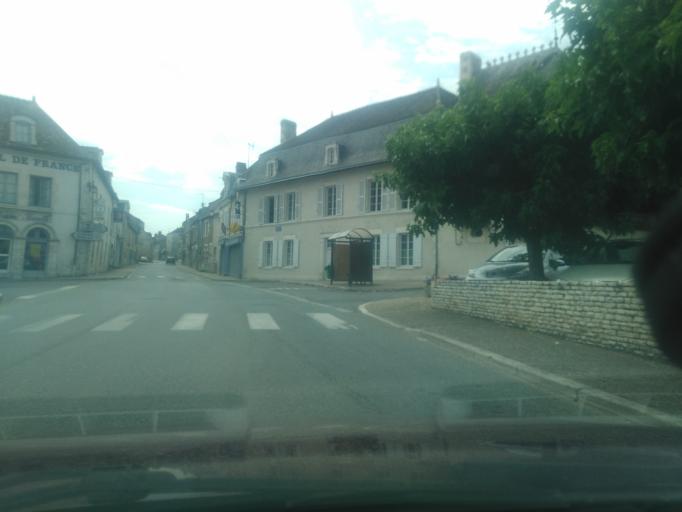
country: FR
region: Poitou-Charentes
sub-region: Departement de la Vienne
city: Saint-Savin
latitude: 46.5659
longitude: 0.8638
